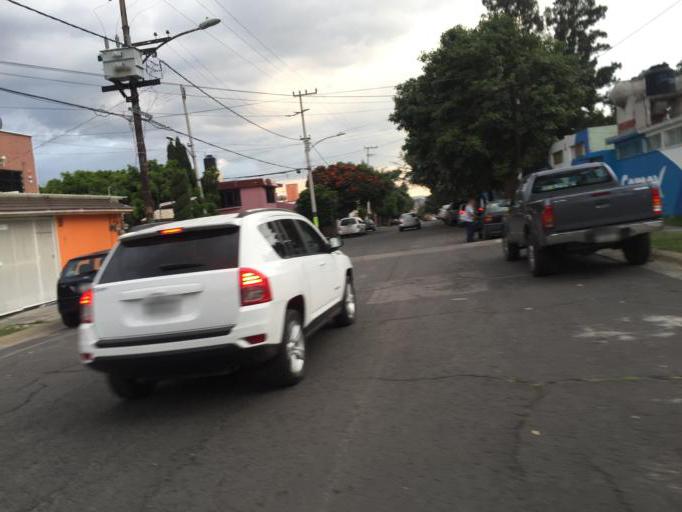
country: MX
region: Mexico
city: Cuautitlan Izcalli
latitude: 19.6515
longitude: -99.2113
